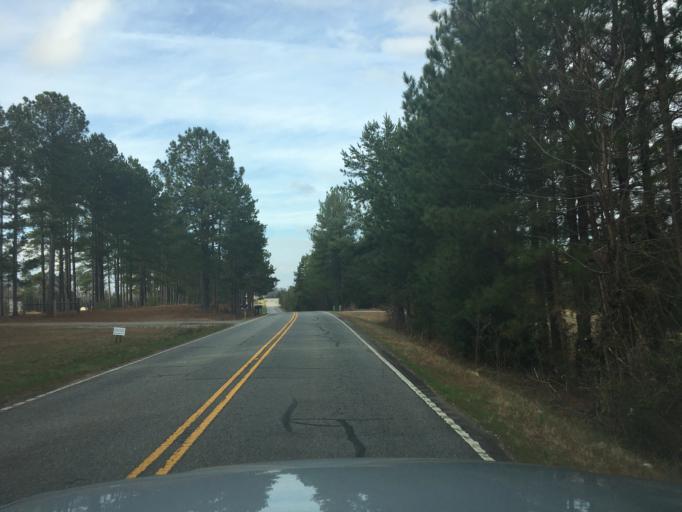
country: US
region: South Carolina
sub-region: Abbeville County
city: Lake Secession
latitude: 34.3687
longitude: -82.5201
